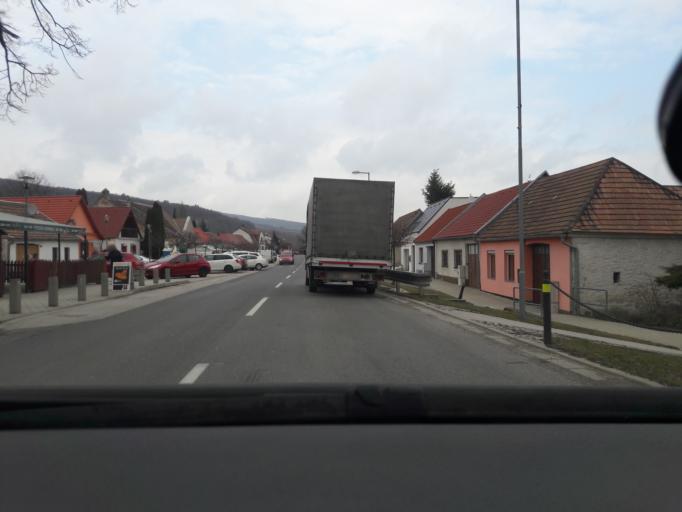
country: SK
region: Bratislavsky
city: Modra
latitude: 48.4001
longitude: 17.3579
